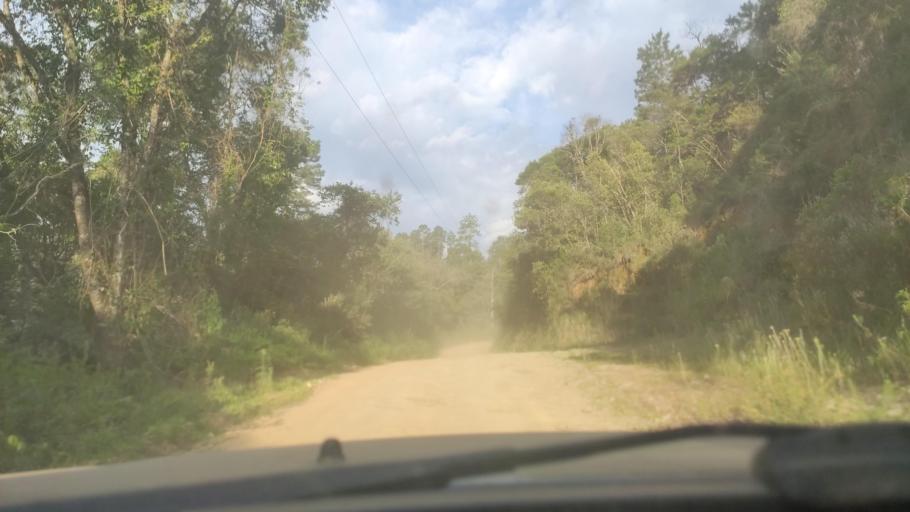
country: BR
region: Minas Gerais
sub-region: Cambui
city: Cambui
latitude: -22.7503
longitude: -45.9300
